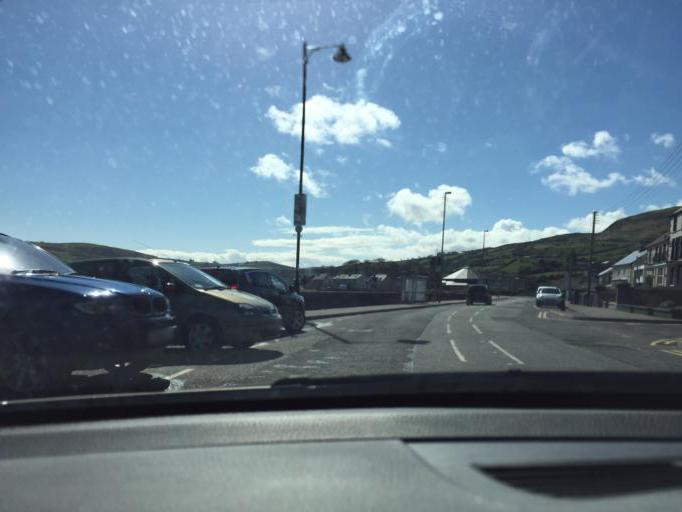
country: GB
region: Northern Ireland
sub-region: Larne District
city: Carnlough
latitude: 54.9914
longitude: -5.9908
